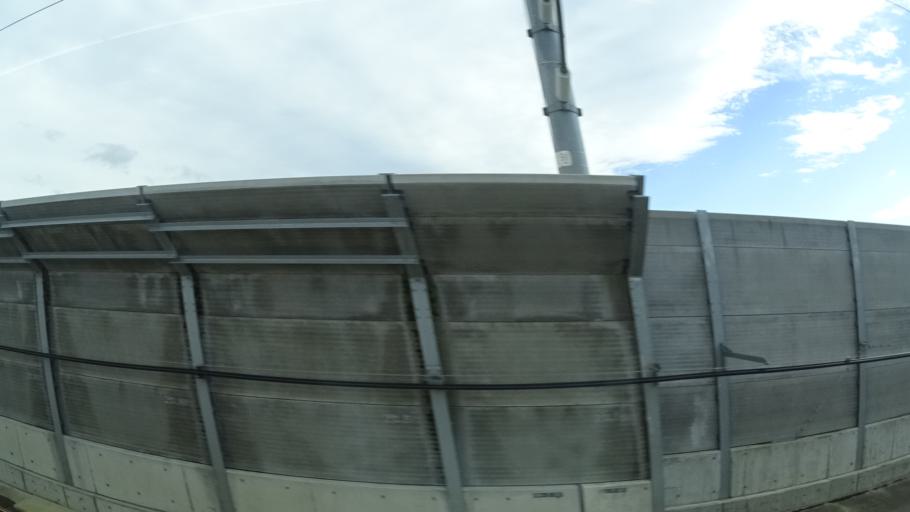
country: JP
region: Toyama
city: Kuragaki-kosugi
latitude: 36.7214
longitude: 137.1606
